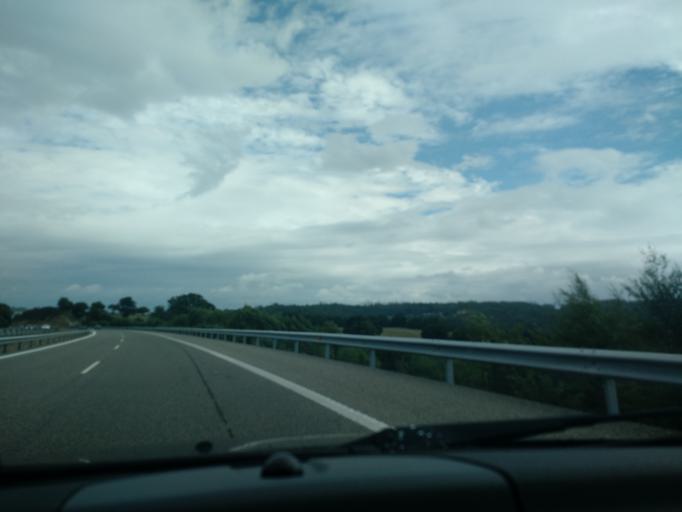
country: ES
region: Galicia
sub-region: Provincia da Coruna
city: Abegondo
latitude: 43.2396
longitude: -8.2571
